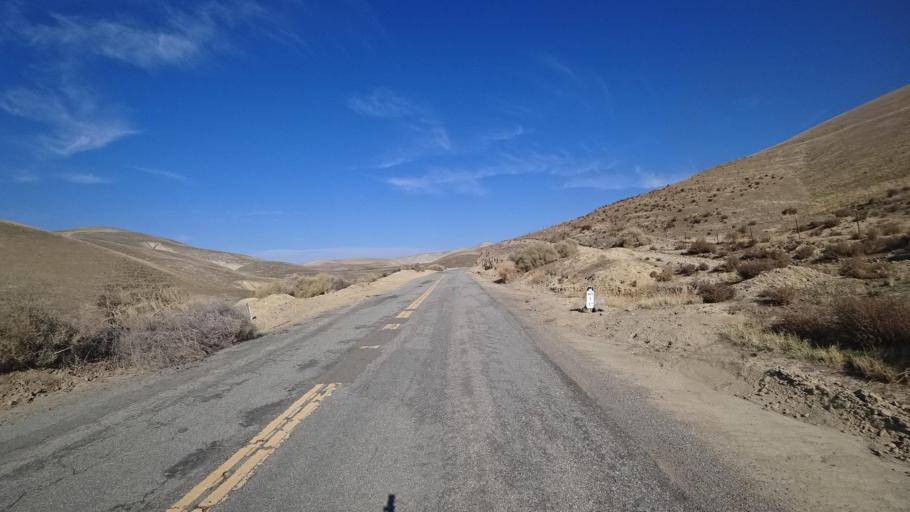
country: US
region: California
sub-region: Kern County
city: Oildale
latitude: 35.4582
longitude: -118.8276
